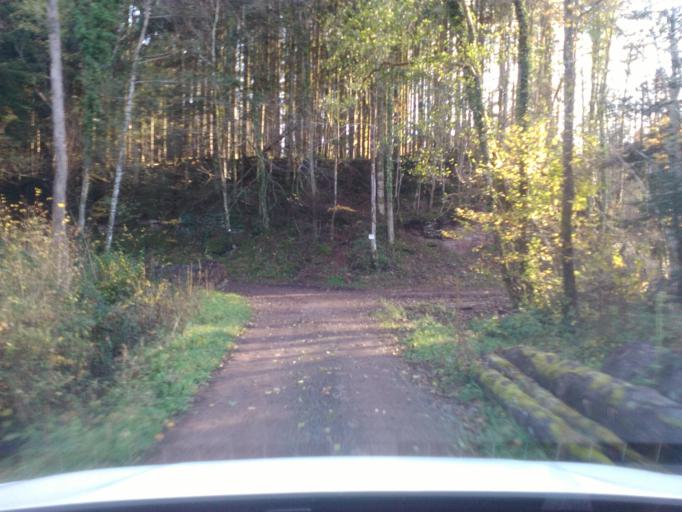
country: FR
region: Lorraine
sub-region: Departement des Vosges
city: Saint-Die-des-Vosges
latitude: 48.3297
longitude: 6.9905
